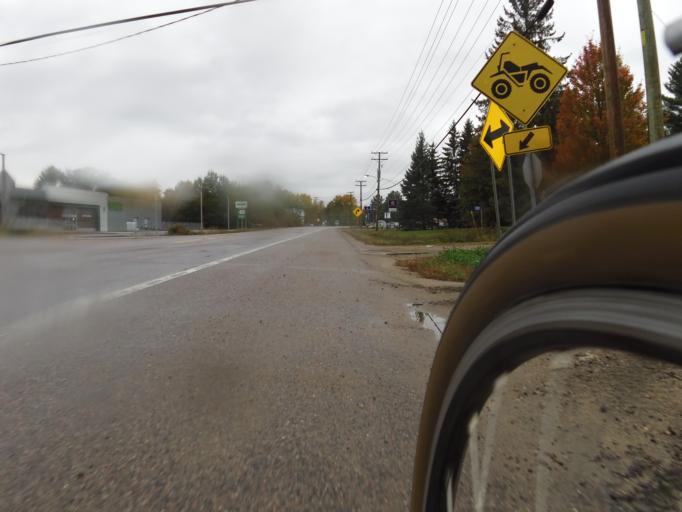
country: CA
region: Quebec
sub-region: Outaouais
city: Fort-Coulonge
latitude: 45.8540
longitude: -76.7363
